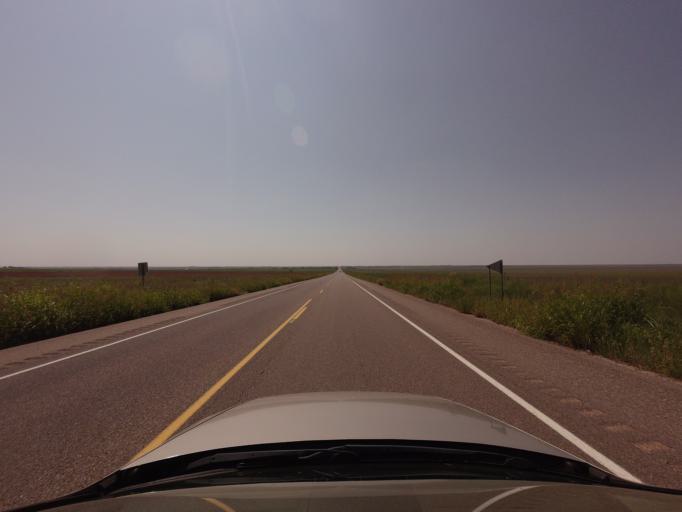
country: US
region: New Mexico
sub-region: Curry County
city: Clovis
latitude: 34.5489
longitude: -103.1965
